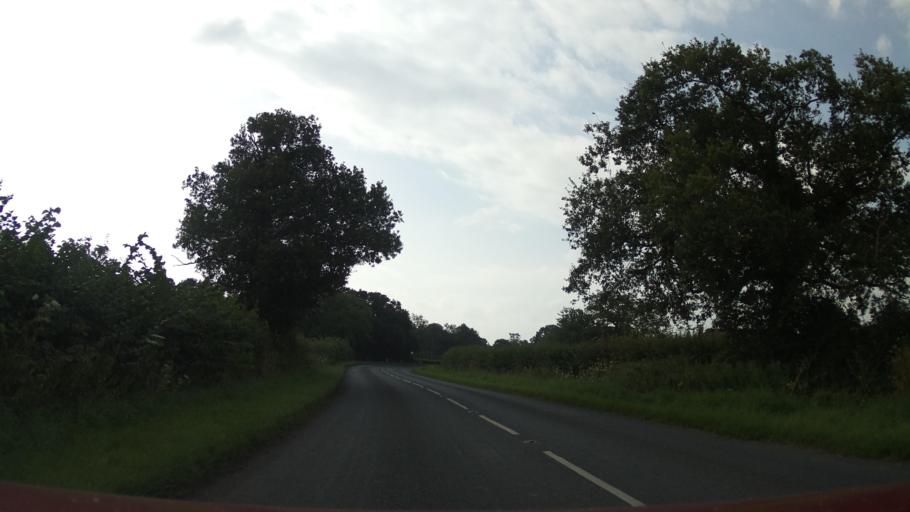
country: GB
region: England
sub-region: Bath and North East Somerset
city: Compton Martin
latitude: 51.3225
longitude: -2.6403
